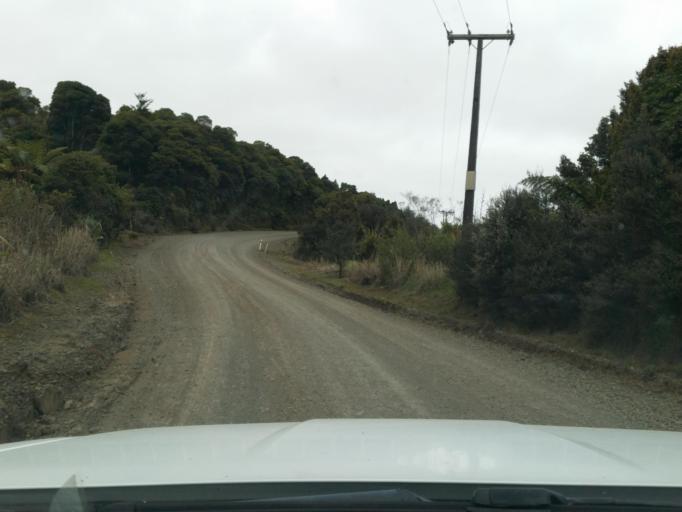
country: NZ
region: Northland
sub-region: Kaipara District
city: Dargaville
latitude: -35.7193
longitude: 173.6441
